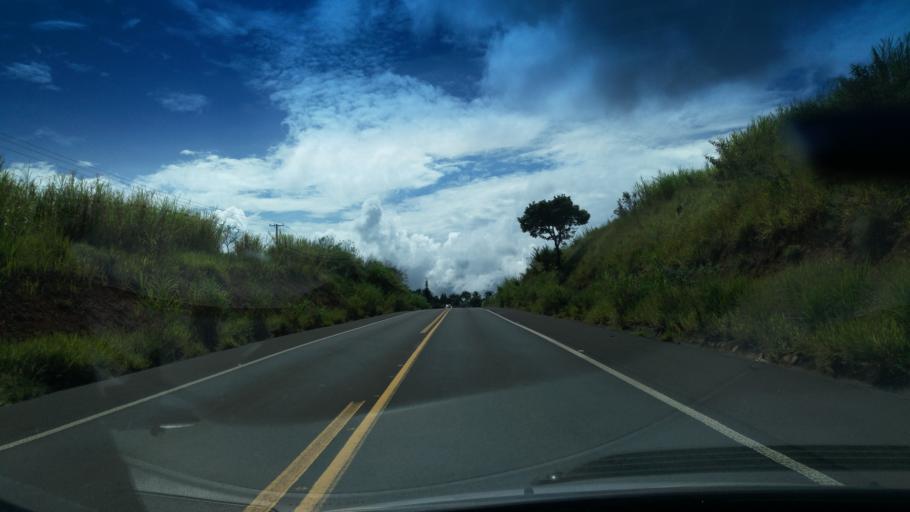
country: BR
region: Sao Paulo
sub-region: Santo Antonio Do Jardim
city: Espirito Santo do Pinhal
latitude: -22.1440
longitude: -46.7143
